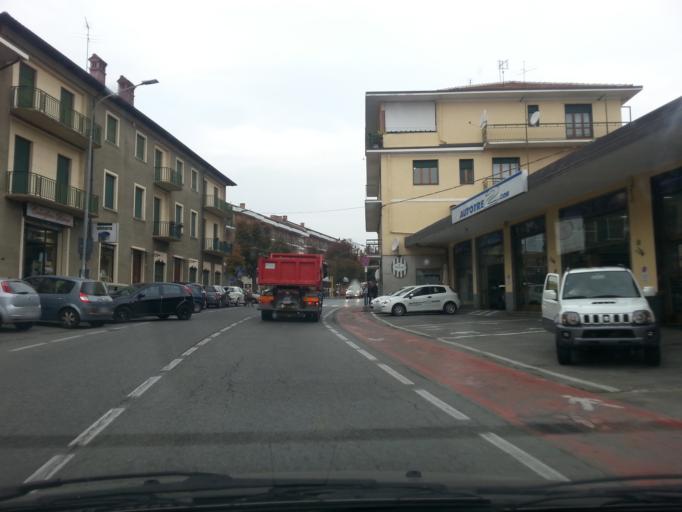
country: IT
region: Piedmont
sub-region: Provincia di Torino
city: Giaveno
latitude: 45.0404
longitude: 7.3555
